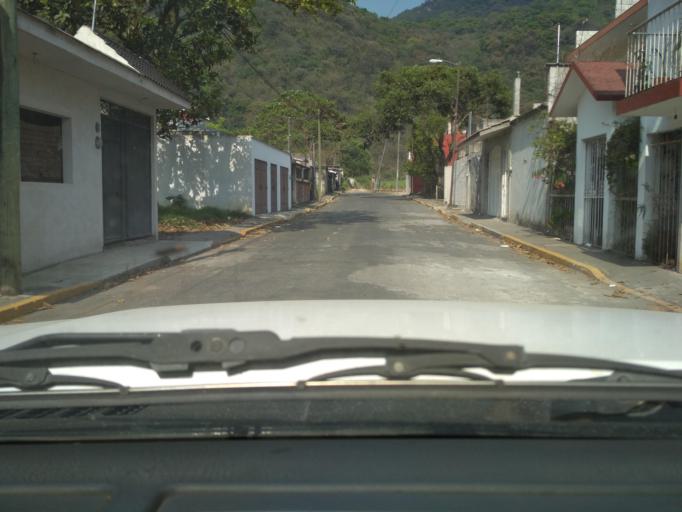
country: MX
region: Veracruz
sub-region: Mariano Escobedo
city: Palmira
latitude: 18.8709
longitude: -97.0954
